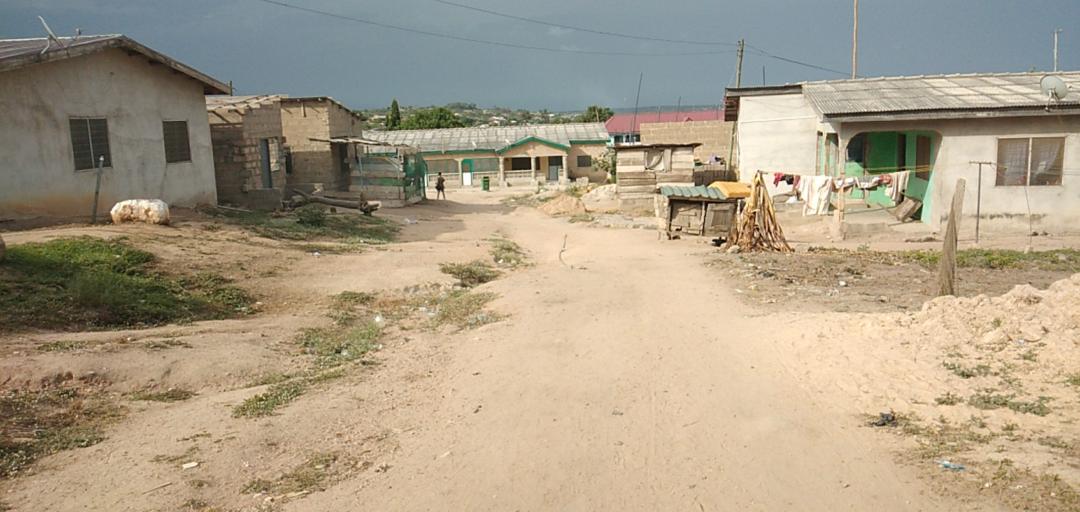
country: GH
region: Central
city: Winneba
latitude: 5.3578
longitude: -0.6182
